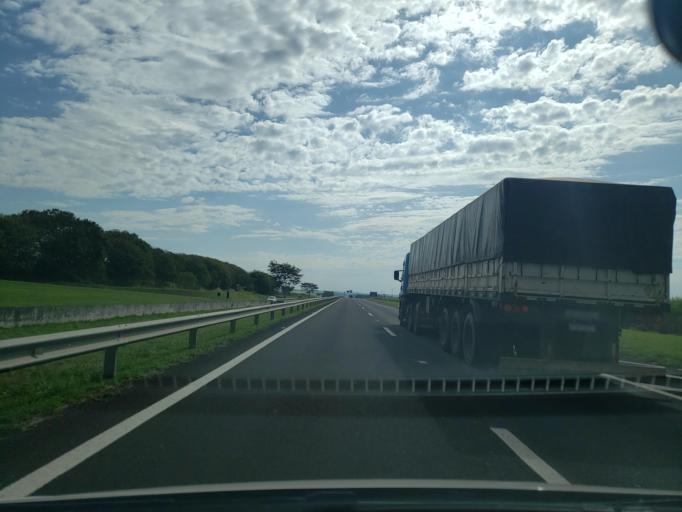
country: BR
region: Sao Paulo
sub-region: Promissao
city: Promissao
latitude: -21.6307
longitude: -49.8403
